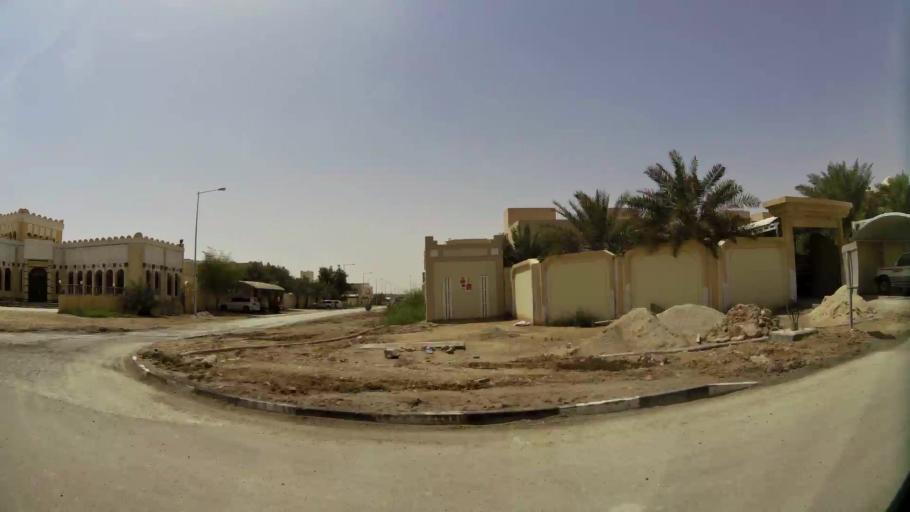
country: QA
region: Baladiyat Umm Salal
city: Umm Salal Muhammad
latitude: 25.3757
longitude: 51.4475
